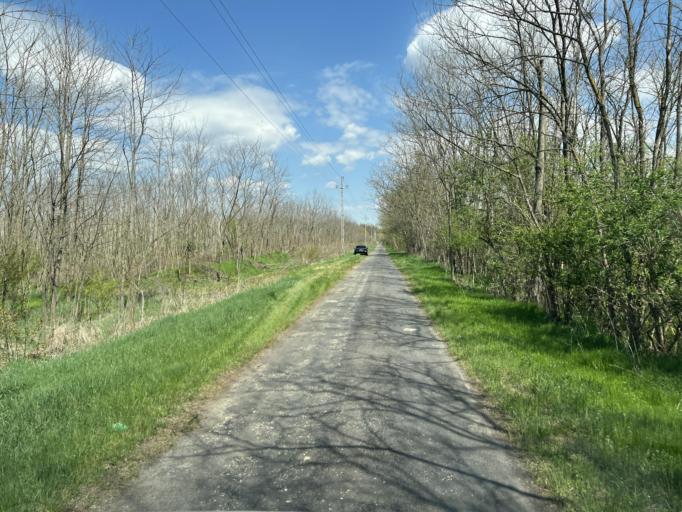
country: HU
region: Pest
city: Kakucs
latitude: 47.2723
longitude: 19.3655
